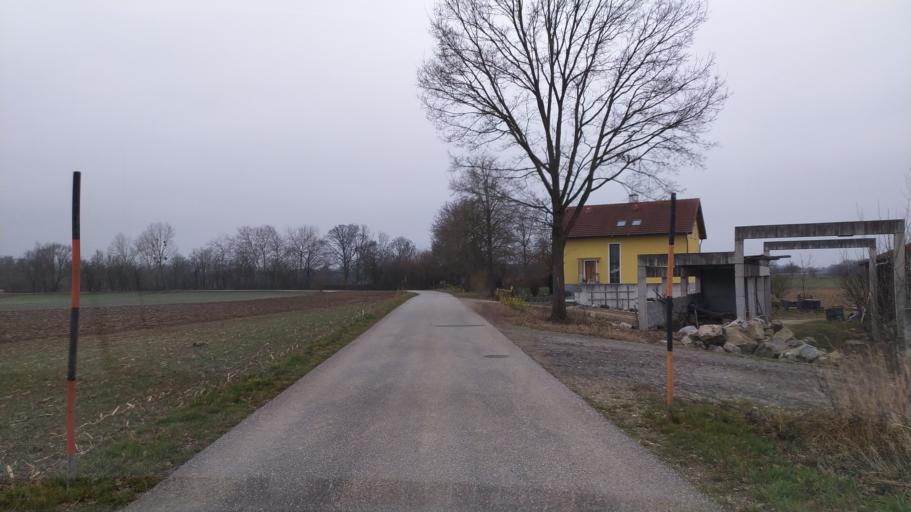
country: AT
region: Upper Austria
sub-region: Politischer Bezirk Perg
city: Perg
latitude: 48.2204
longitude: 14.7214
